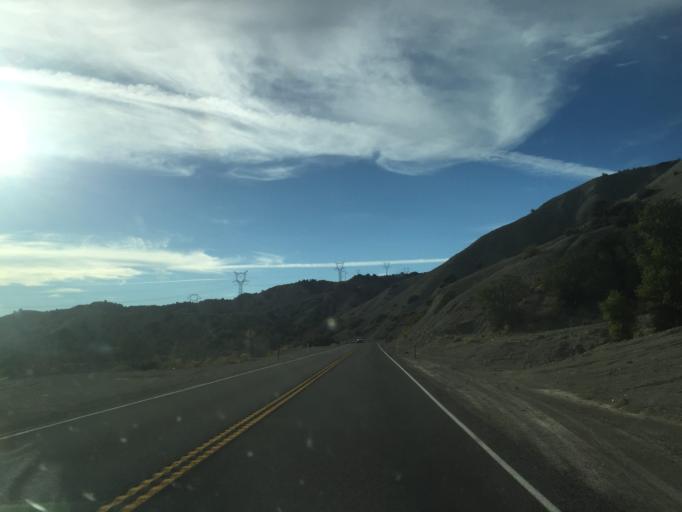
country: US
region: Utah
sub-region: Juab County
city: Nephi
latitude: 39.7184
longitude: -111.7551
